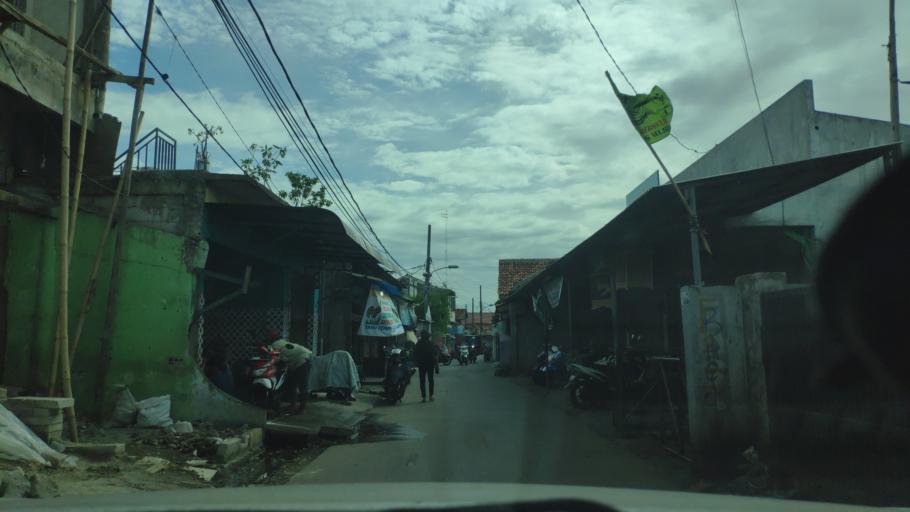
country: ID
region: West Java
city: Ciputat
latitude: -6.2226
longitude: 106.7131
